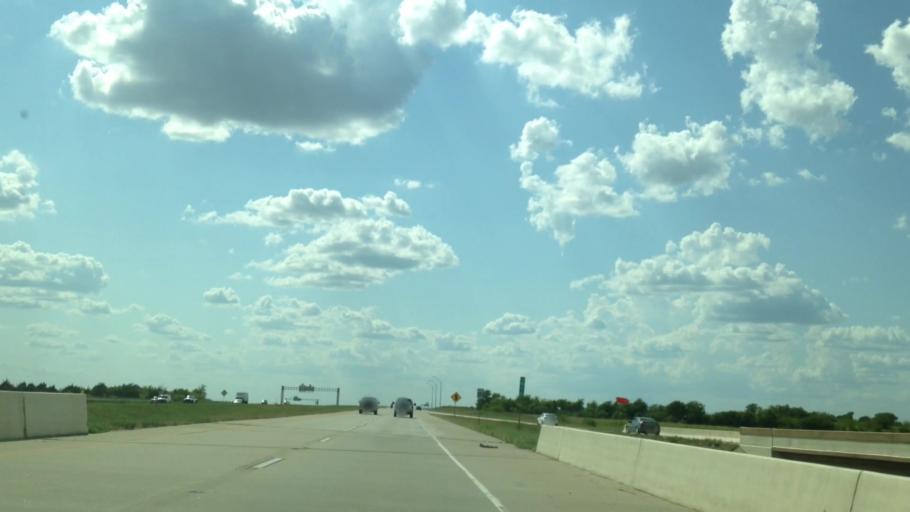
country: US
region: Texas
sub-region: Travis County
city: Onion Creek
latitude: 30.0810
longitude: -97.7012
